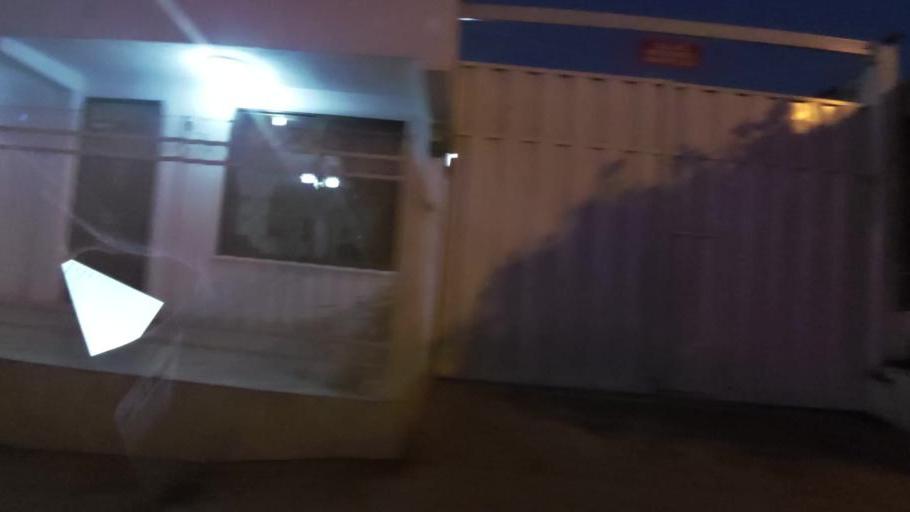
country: CO
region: Bolivar
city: Cartagena
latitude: 10.4040
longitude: -75.5098
